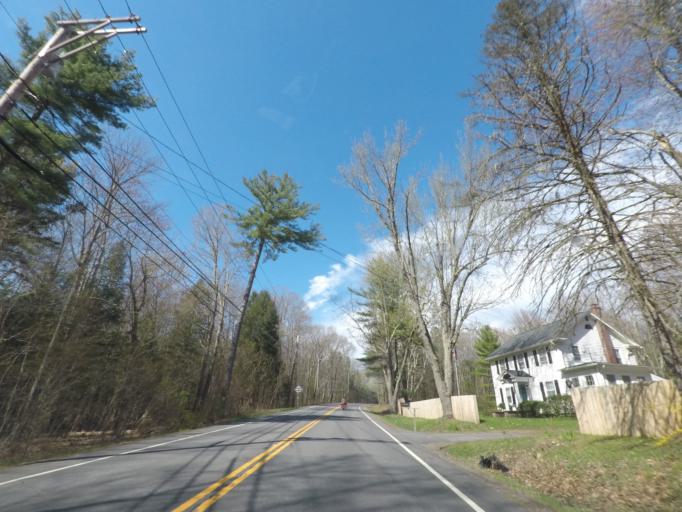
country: US
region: New York
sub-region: Greene County
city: Cairo
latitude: 42.3652
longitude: -74.0424
